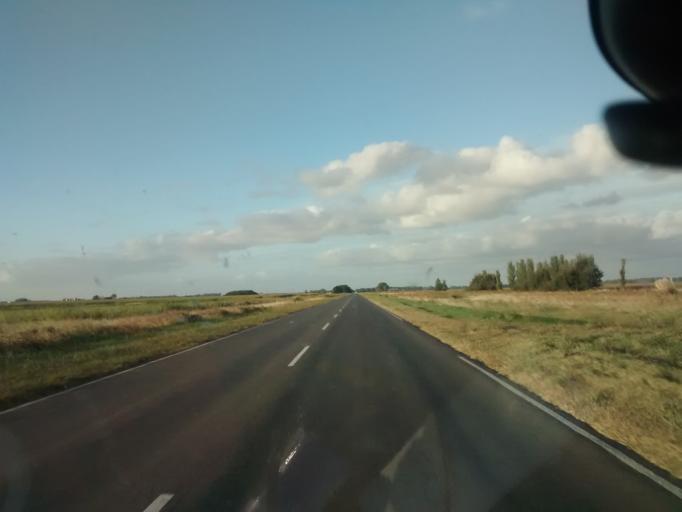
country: AR
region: Buenos Aires
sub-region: Partido de General Belgrano
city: General Belgrano
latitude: -35.8233
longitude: -58.5754
